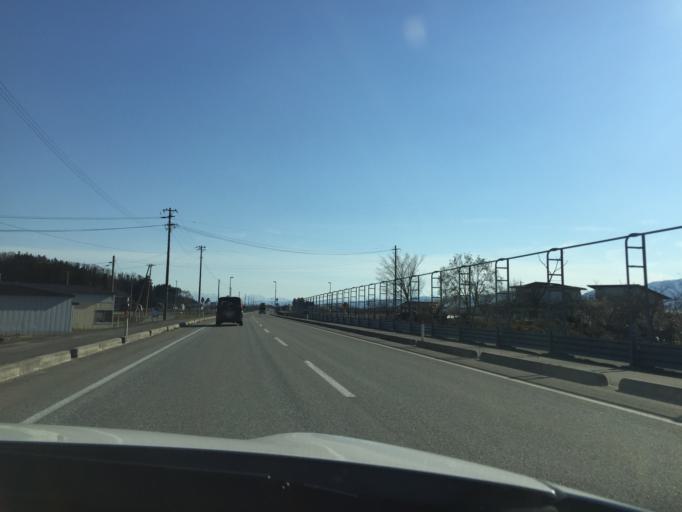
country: JP
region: Yamagata
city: Nagai
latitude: 38.1455
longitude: 140.0613
